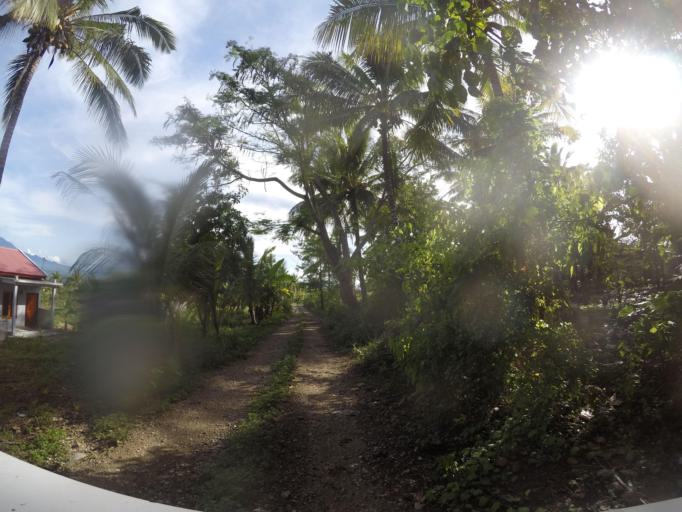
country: TL
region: Baucau
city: Baucau
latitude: -8.5071
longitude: 126.4472
